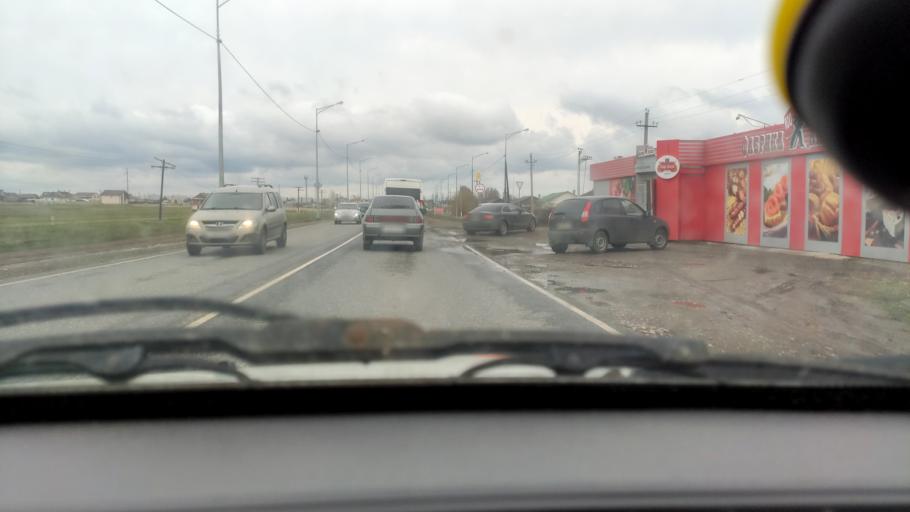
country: RU
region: Samara
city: Zhigulevsk
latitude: 53.5444
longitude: 49.5172
